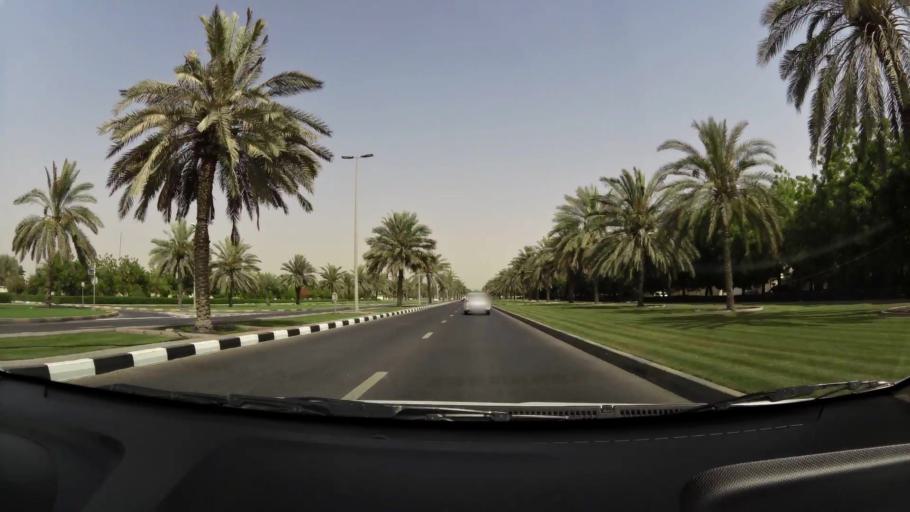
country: AE
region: Ash Shariqah
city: Sharjah
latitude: 25.3366
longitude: 55.4363
